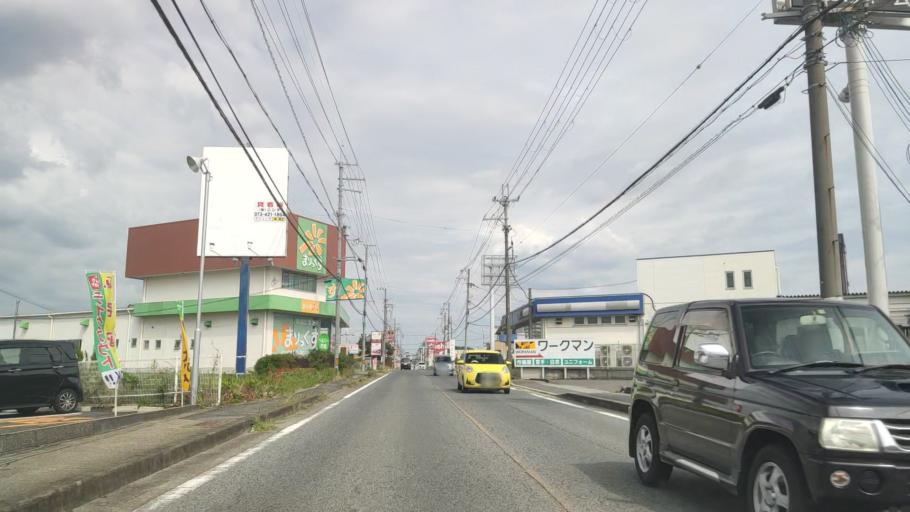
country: JP
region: Wakayama
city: Hashimoto
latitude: 34.3072
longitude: 135.5729
